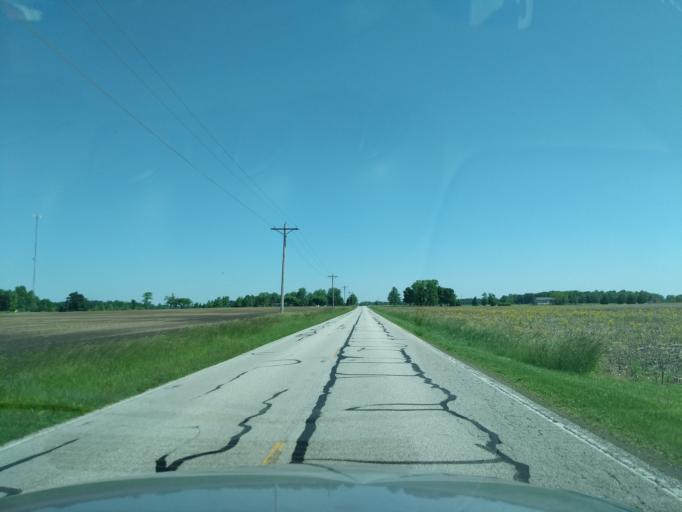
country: US
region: Indiana
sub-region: Huntington County
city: Warren
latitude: 40.6930
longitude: -85.5069
